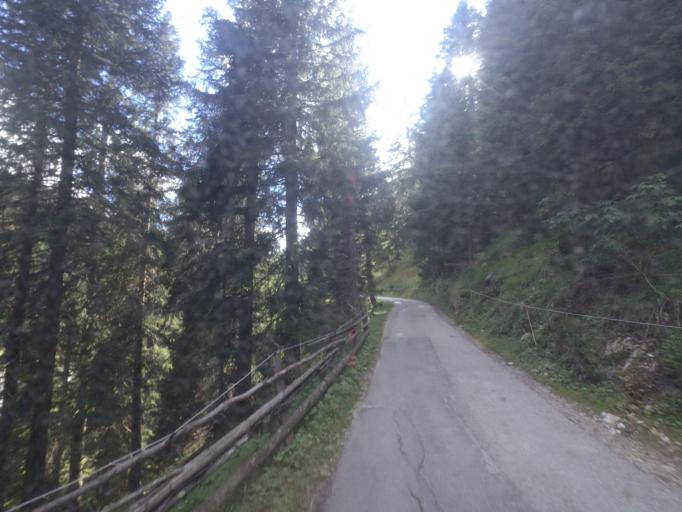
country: AT
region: Salzburg
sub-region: Politischer Bezirk Sankt Johann im Pongau
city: Kleinarl
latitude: 47.1821
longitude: 13.3558
